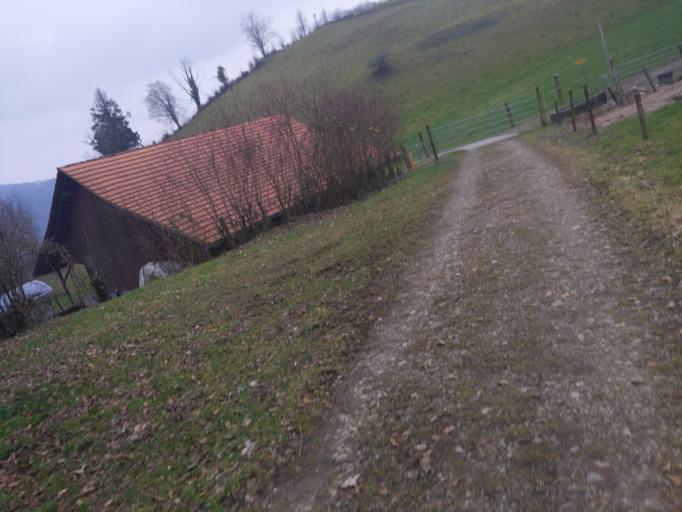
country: CH
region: Saint Gallen
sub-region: Wahlkreis See-Gaster
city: Eschenbach
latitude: 47.2257
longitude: 8.9091
